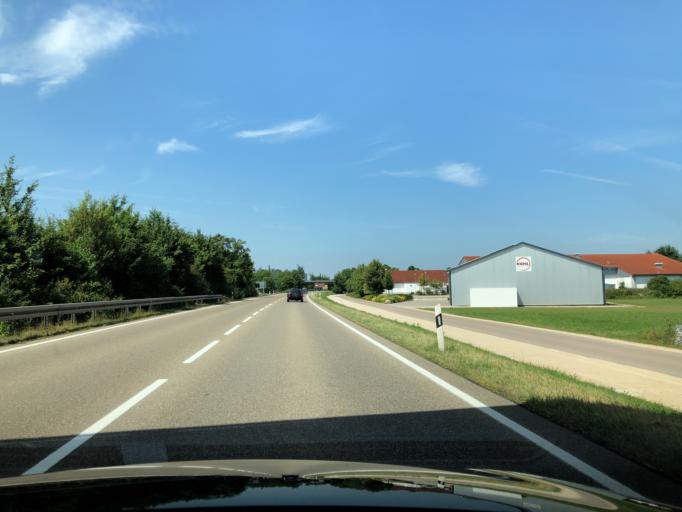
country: DE
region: Bavaria
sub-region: Swabia
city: Niederschonenfeld
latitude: 48.7034
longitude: 10.9308
